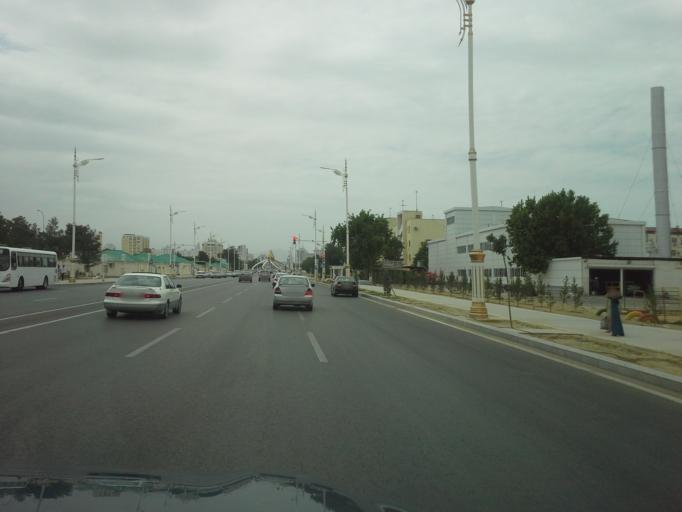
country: TM
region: Ahal
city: Ashgabat
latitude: 37.9205
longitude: 58.3963
